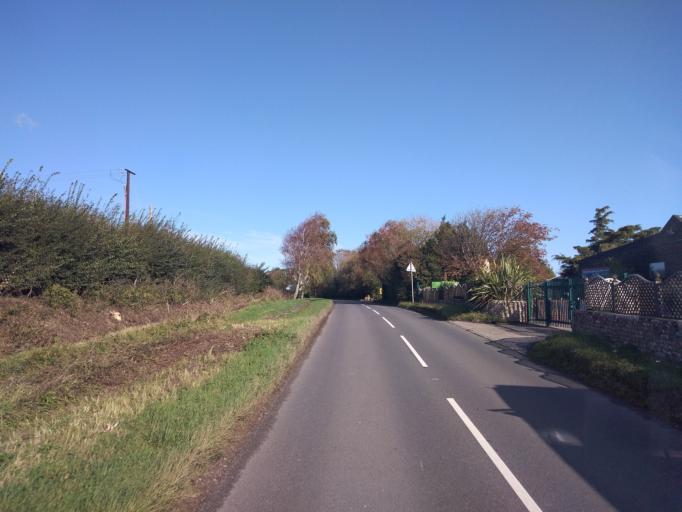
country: GB
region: England
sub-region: East Sussex
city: Seaford
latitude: 50.8234
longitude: 0.1623
